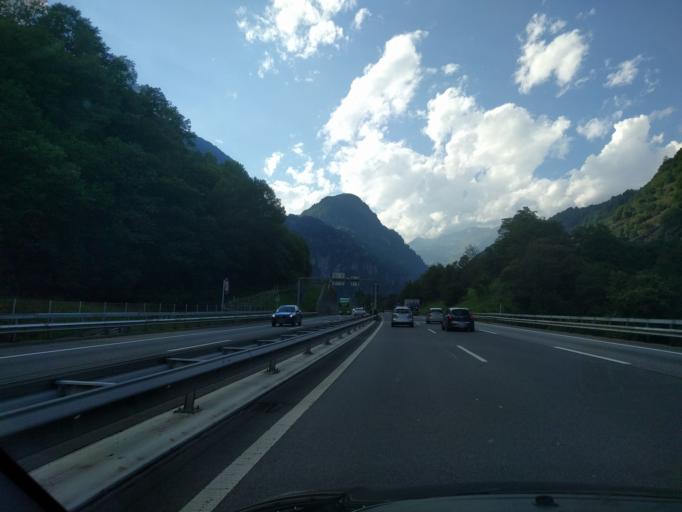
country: CH
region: Ticino
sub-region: Blenio District
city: Cancori
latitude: 46.4335
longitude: 8.8492
